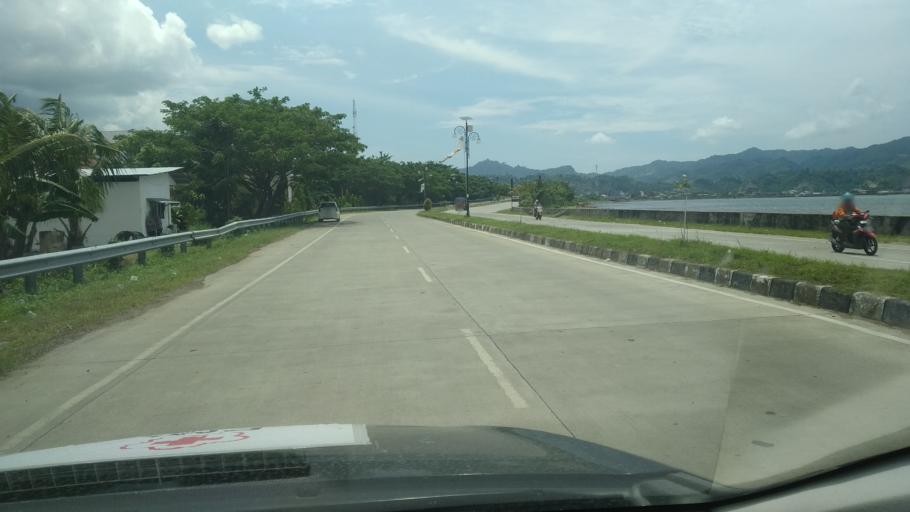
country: ID
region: Sulawesi Barat
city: Mamuju
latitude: -2.6771
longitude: 118.8821
